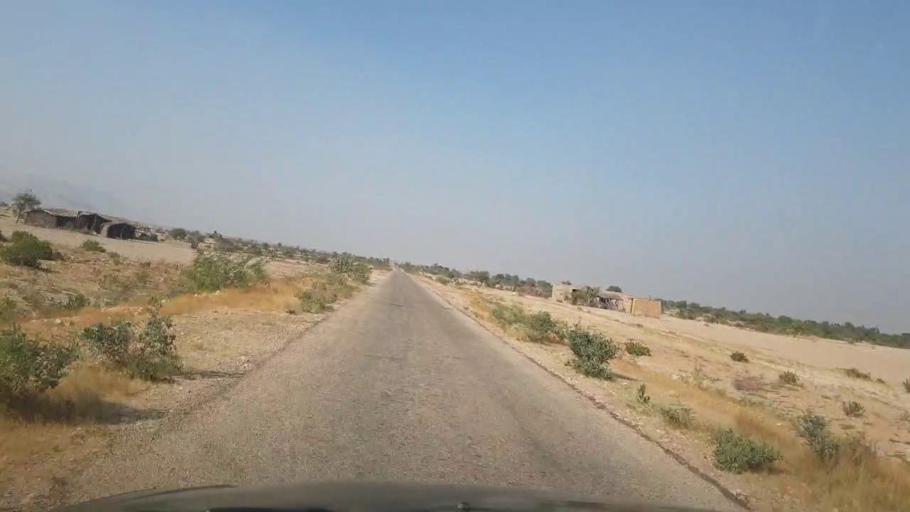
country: PK
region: Sindh
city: Jamshoro
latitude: 25.5837
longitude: 67.8206
